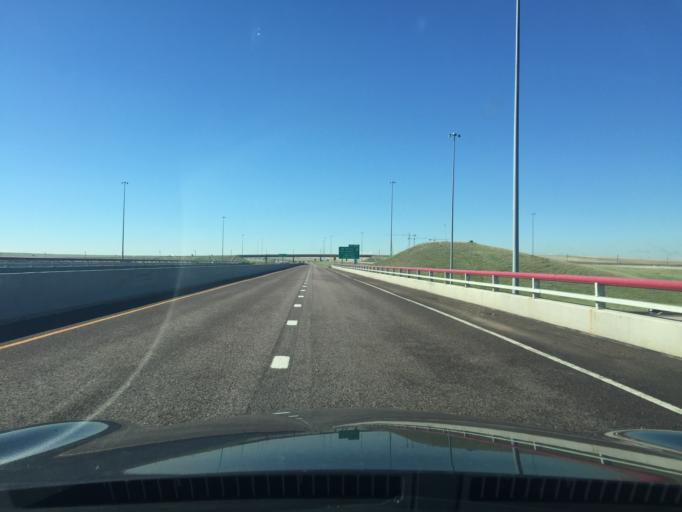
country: US
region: Colorado
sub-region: Adams County
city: Aurora
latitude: 39.8349
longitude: -104.7473
